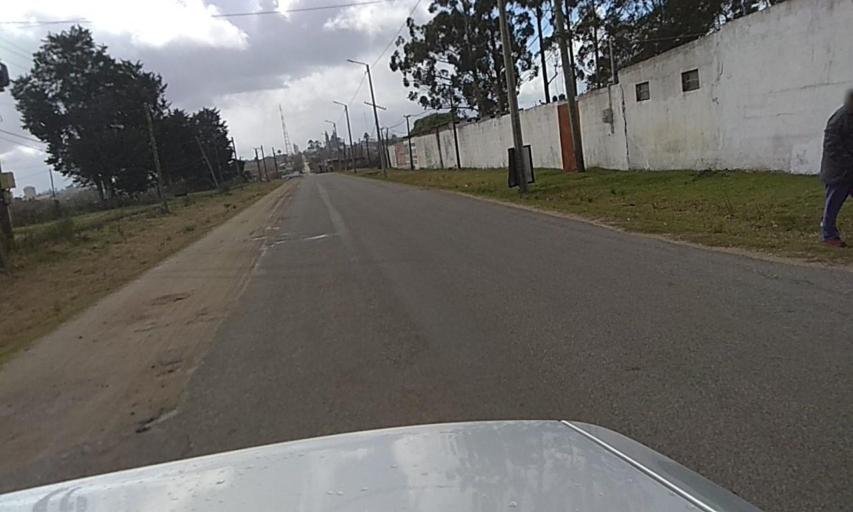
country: UY
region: Florida
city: Florida
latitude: -34.1095
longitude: -56.2253
